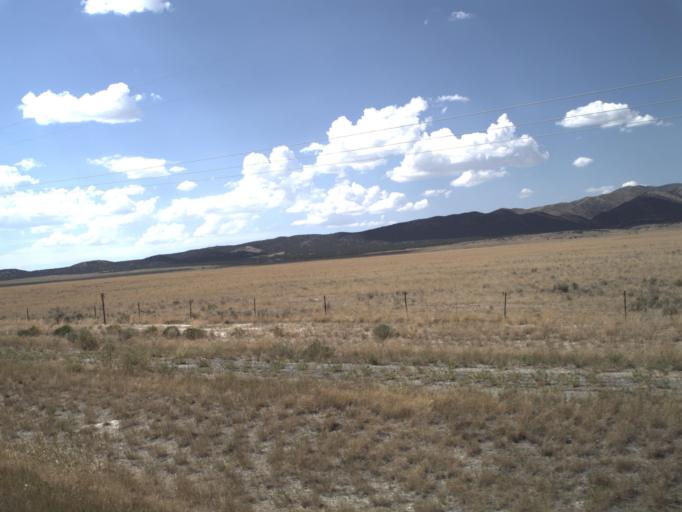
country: US
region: Idaho
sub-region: Power County
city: American Falls
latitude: 41.9677
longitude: -113.0893
